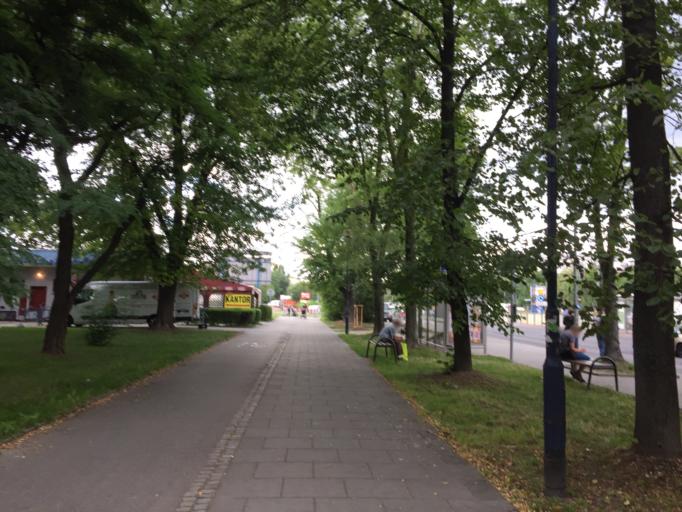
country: PL
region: Lesser Poland Voivodeship
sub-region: Powiat wielicki
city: Kokotow
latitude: 50.0786
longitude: 20.0283
